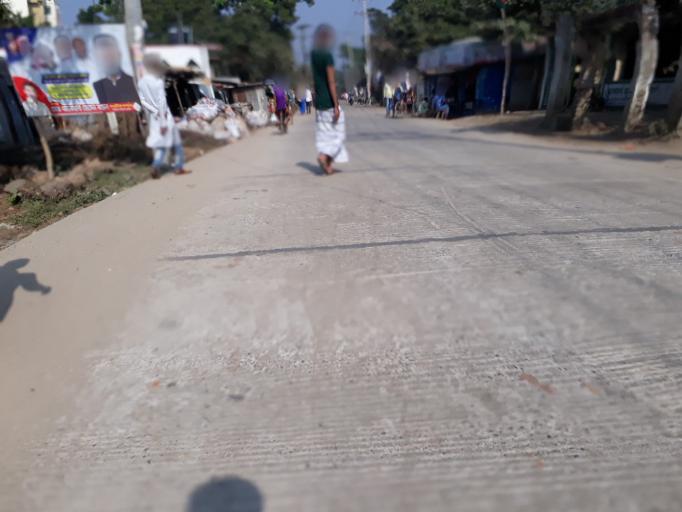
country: BD
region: Dhaka
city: Tungi
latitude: 23.8828
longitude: 90.3102
